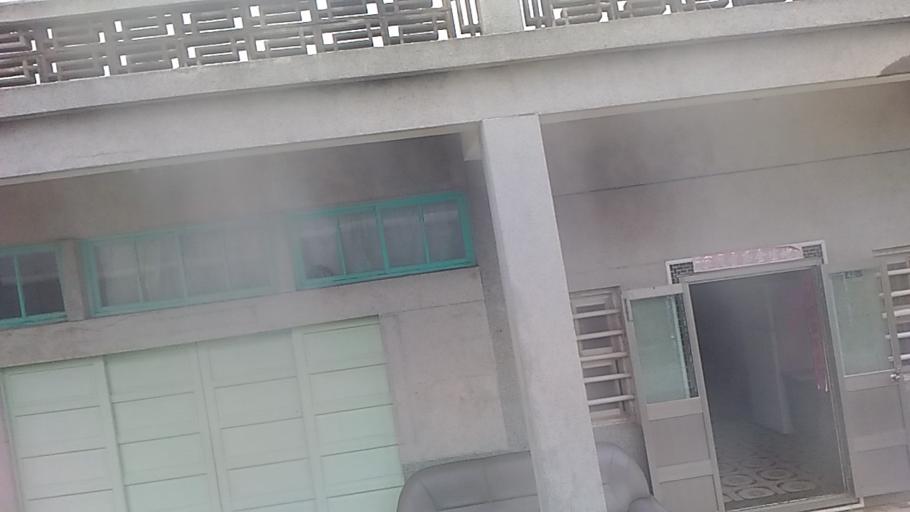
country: TW
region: Taiwan
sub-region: Penghu
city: Ma-kung
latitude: 23.2052
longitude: 119.4329
